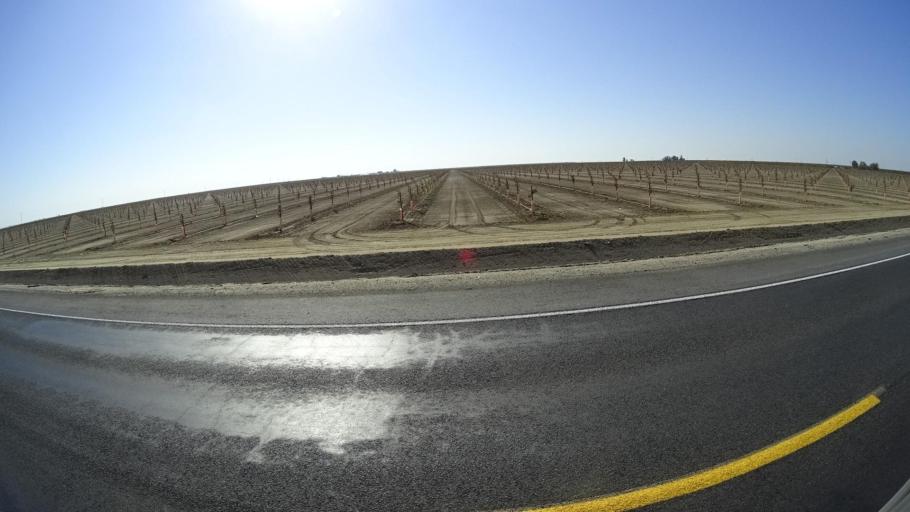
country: US
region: California
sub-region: Kern County
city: Delano
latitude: 35.7178
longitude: -119.3063
